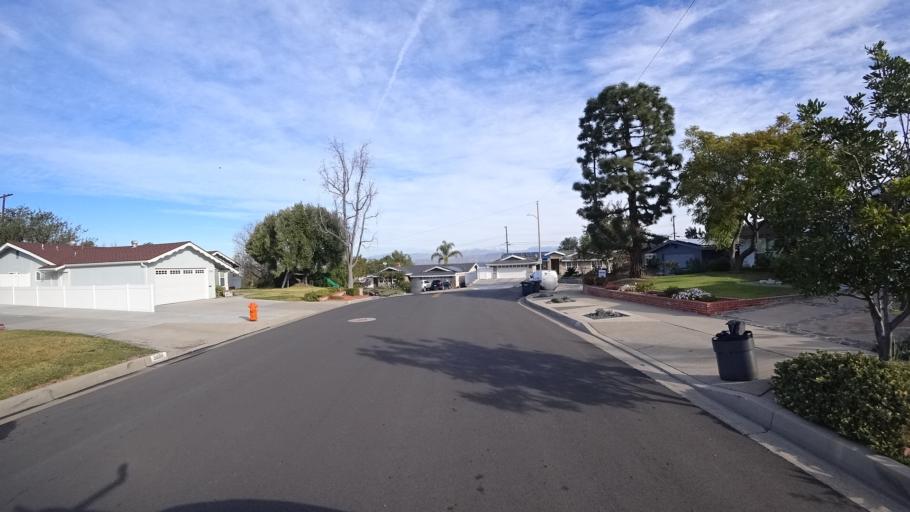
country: US
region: California
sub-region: Orange County
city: Villa Park
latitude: 33.8401
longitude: -117.8383
